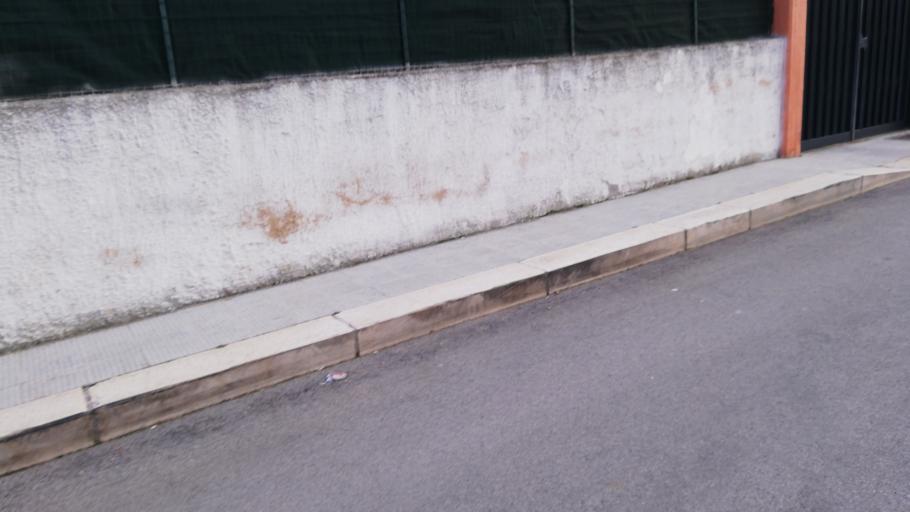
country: IT
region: Apulia
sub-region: Provincia di Barletta - Andria - Trani
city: Andria
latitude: 41.2398
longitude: 16.2960
